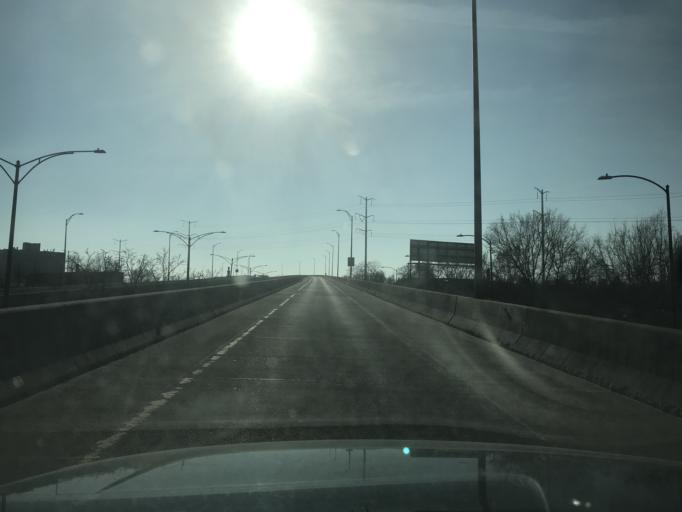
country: US
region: Illinois
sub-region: Cook County
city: Chicago
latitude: 41.7538
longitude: -87.5861
